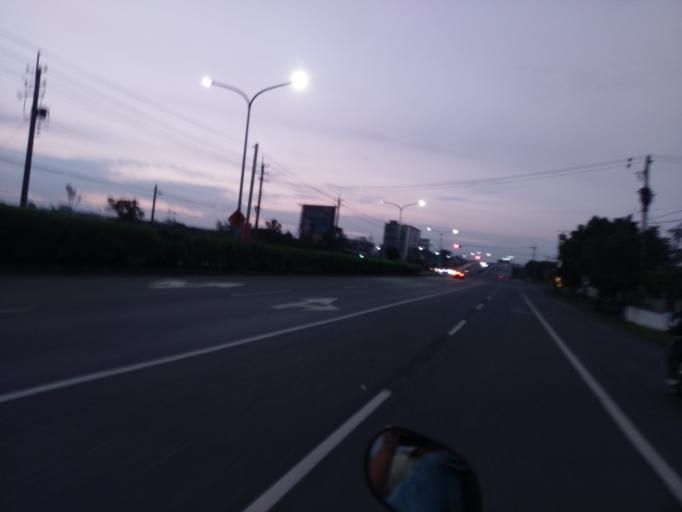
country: TW
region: Taiwan
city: Xinying
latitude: 23.1950
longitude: 120.3228
